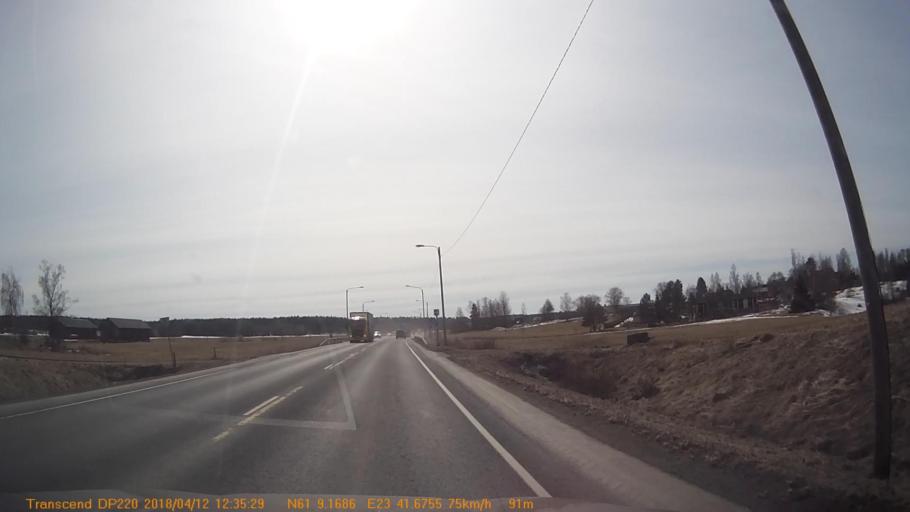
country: FI
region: Pirkanmaa
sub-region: Etelae-Pirkanmaa
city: Kylmaekoski
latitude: 61.1530
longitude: 23.6946
